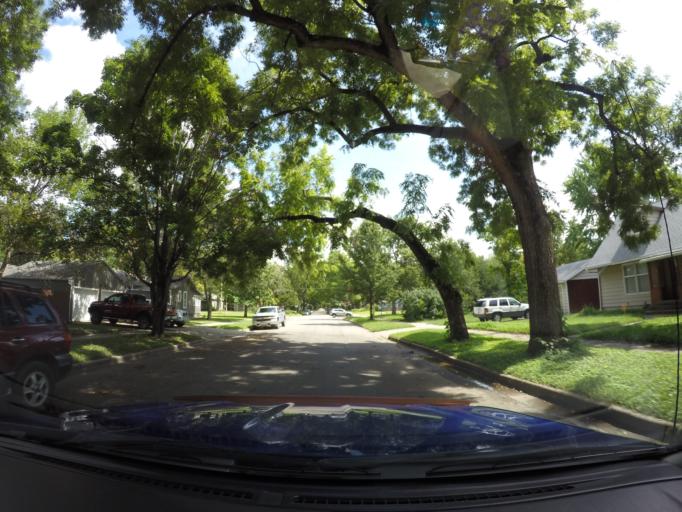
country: US
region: Kansas
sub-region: Riley County
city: Manhattan
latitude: 39.1763
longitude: -96.5774
